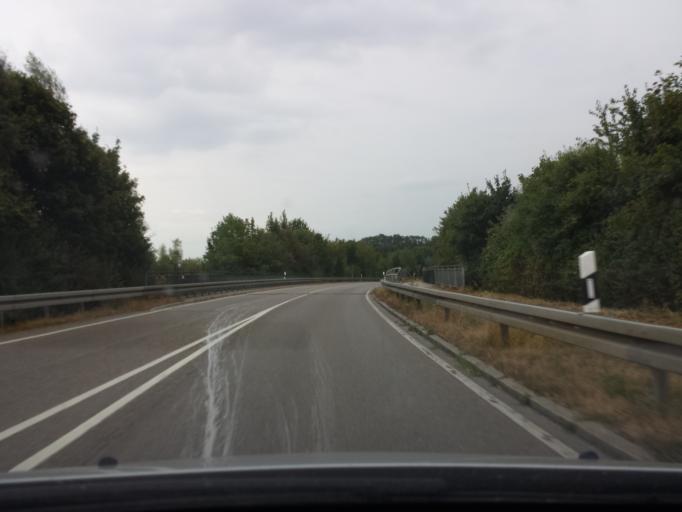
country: DE
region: Bavaria
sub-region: Swabia
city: Holzheim
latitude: 48.4091
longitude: 10.0829
